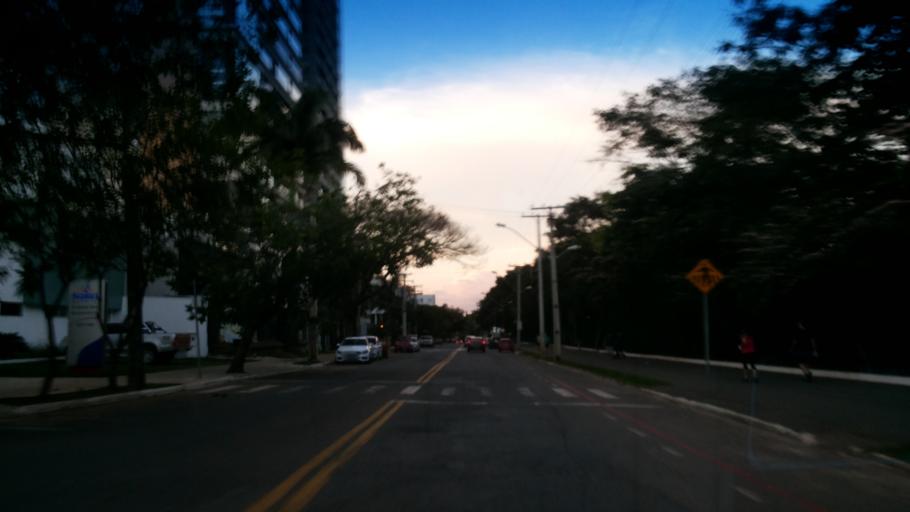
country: BR
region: Goias
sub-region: Goiania
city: Goiania
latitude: -16.7049
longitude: -49.2557
